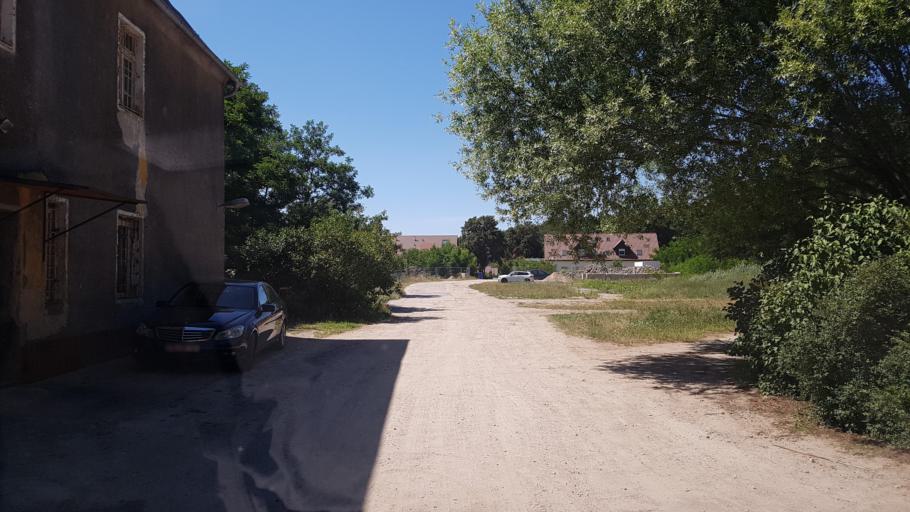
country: DE
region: Brandenburg
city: Trebbin
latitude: 52.2418
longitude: 13.1499
